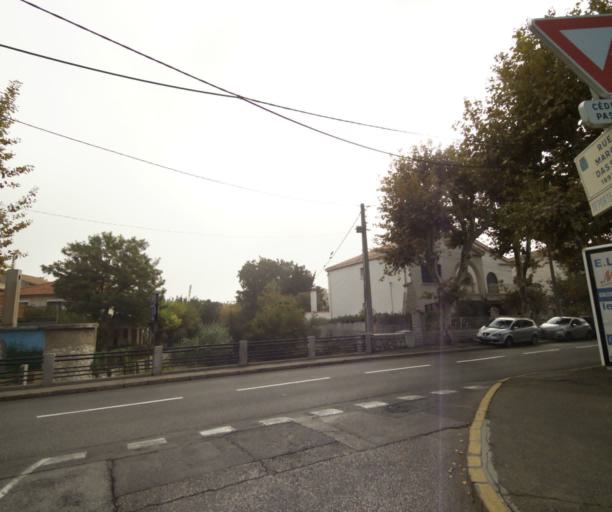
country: FR
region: Provence-Alpes-Cote d'Azur
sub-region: Departement des Bouches-du-Rhone
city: Marignane
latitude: 43.4156
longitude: 5.2166
